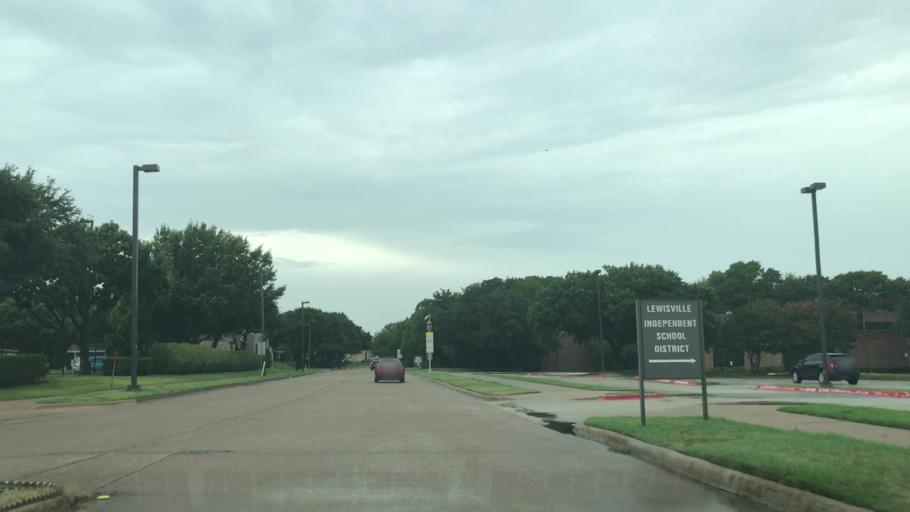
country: US
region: Texas
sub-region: Denton County
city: Highland Village
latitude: 33.0432
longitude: -97.0559
